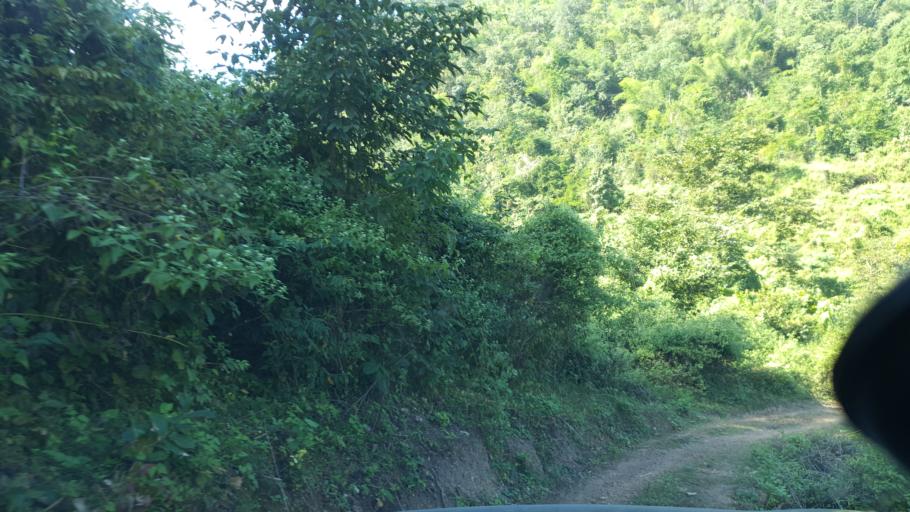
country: TH
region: Mae Hong Son
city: Mae Hi
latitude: 19.3057
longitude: 98.6993
